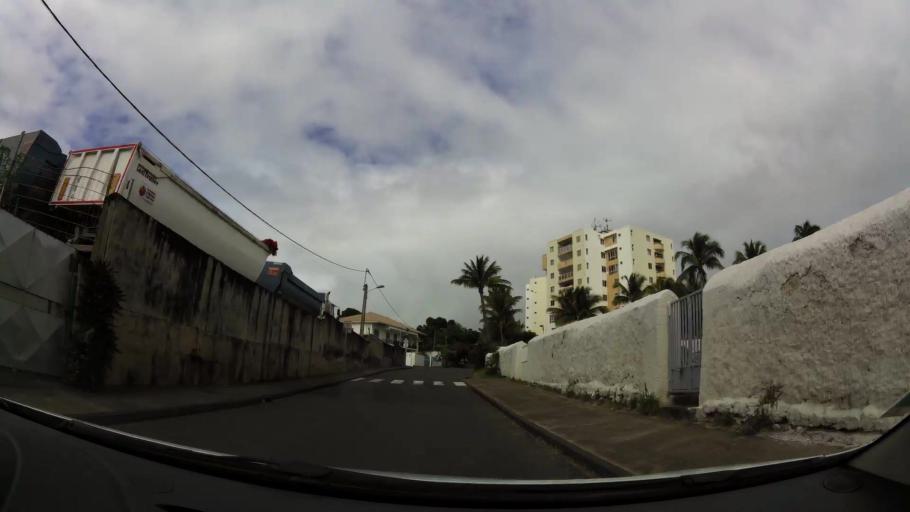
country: RE
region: Reunion
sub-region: Reunion
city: Sainte-Marie
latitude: -20.8972
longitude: 55.5562
